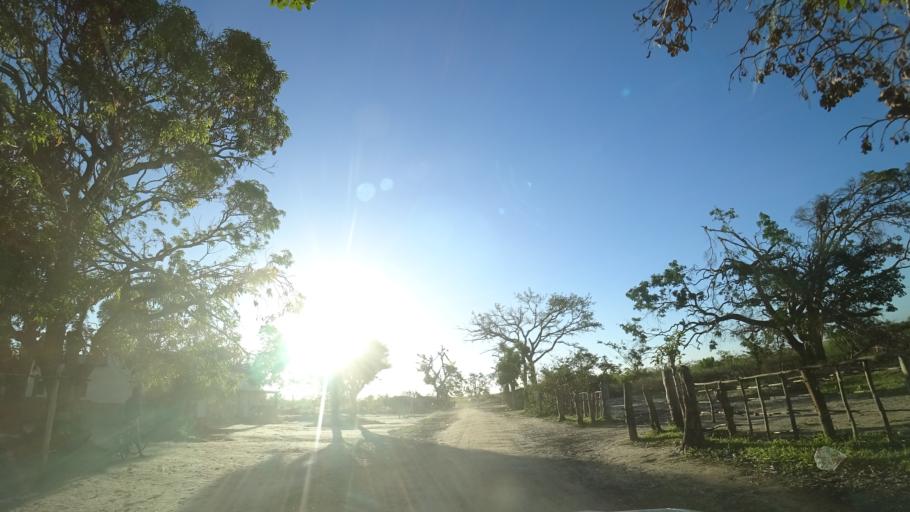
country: MZ
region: Sofala
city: Dondo
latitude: -19.5786
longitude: 35.1191
